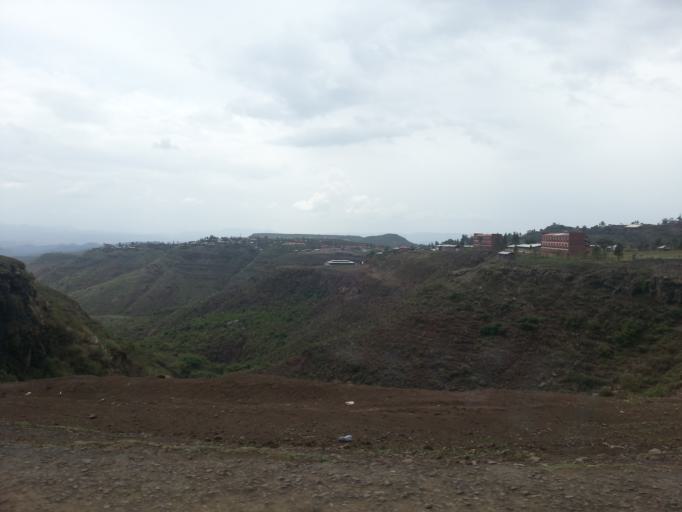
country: ET
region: Amhara
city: Lalibela
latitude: 12.0232
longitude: 39.0525
